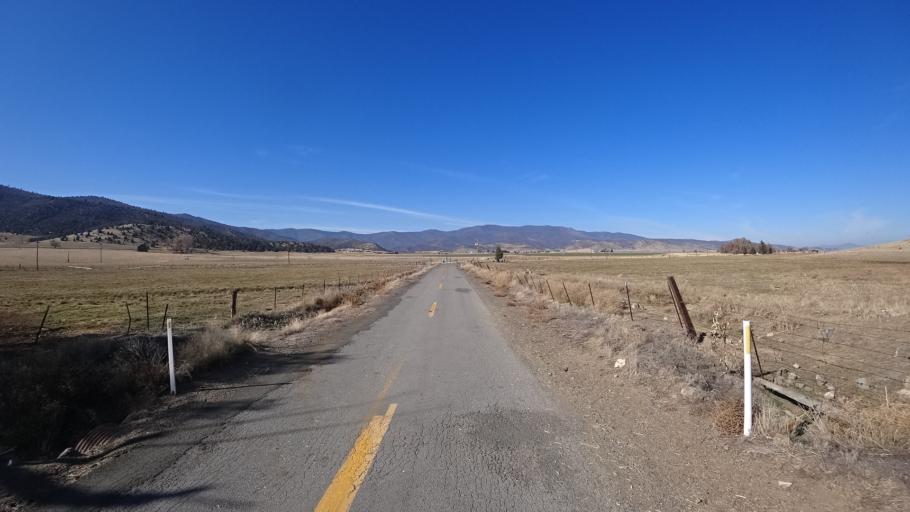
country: US
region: California
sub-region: Siskiyou County
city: Weed
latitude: 41.5279
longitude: -122.5334
